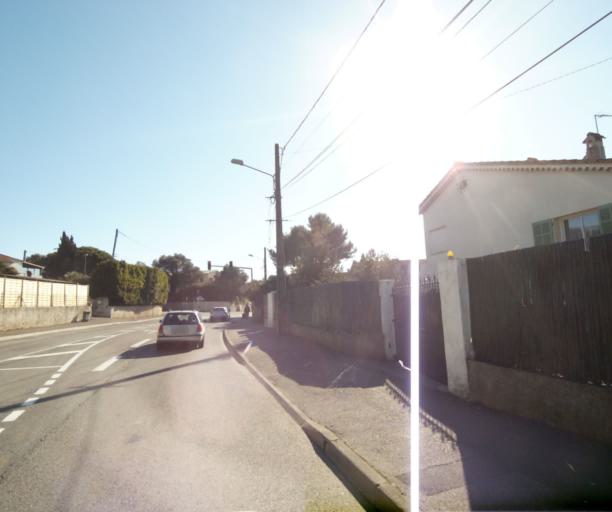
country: FR
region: Provence-Alpes-Cote d'Azur
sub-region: Departement des Alpes-Maritimes
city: Biot
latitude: 43.5977
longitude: 7.1041
